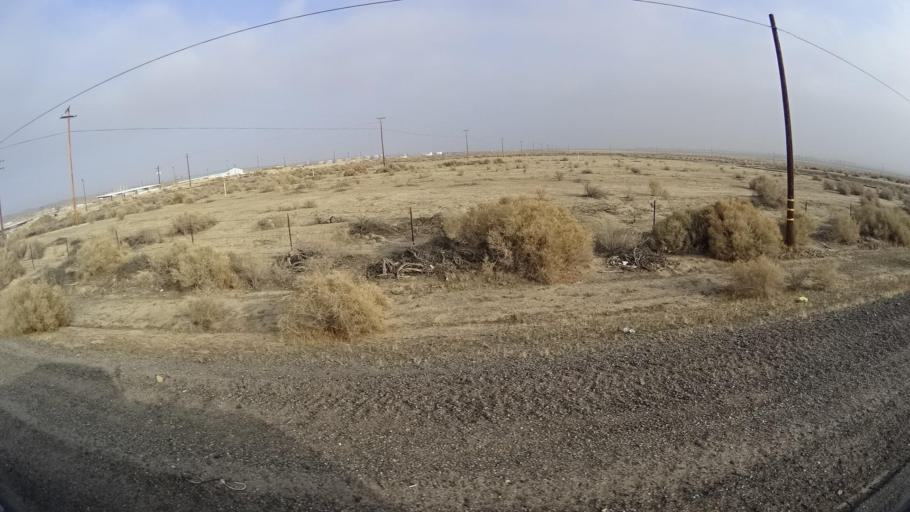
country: US
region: California
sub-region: Kern County
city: Ford City
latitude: 35.2299
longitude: -119.4456
